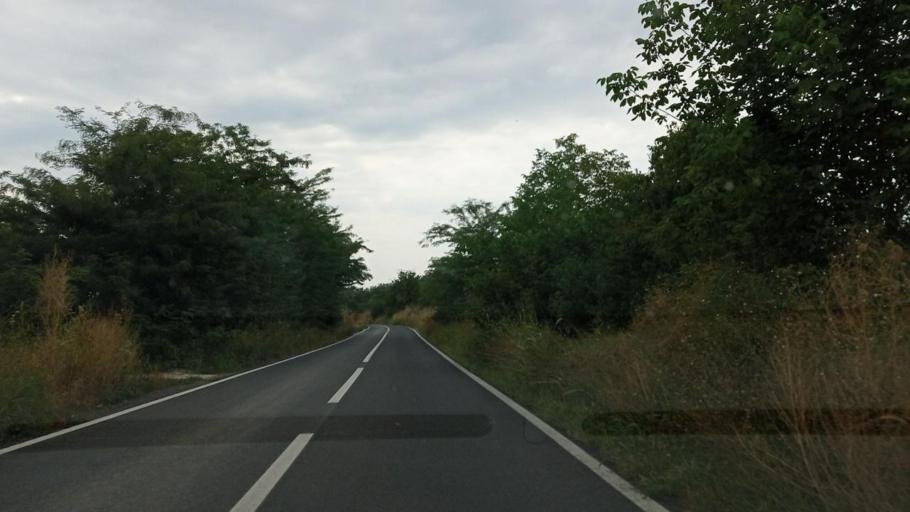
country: RO
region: Giurgiu
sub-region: Comuna Izvoarele
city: Isvoarele
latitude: 44.1694
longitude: 26.2712
